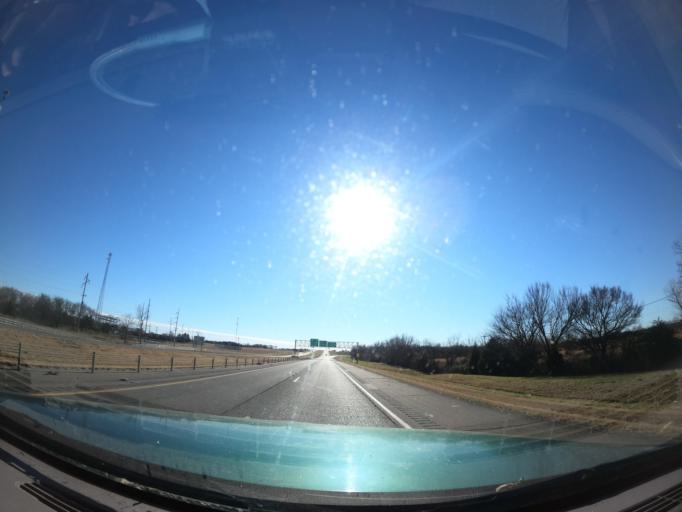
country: US
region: Oklahoma
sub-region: McIntosh County
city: Checotah
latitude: 35.4661
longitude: -95.5407
